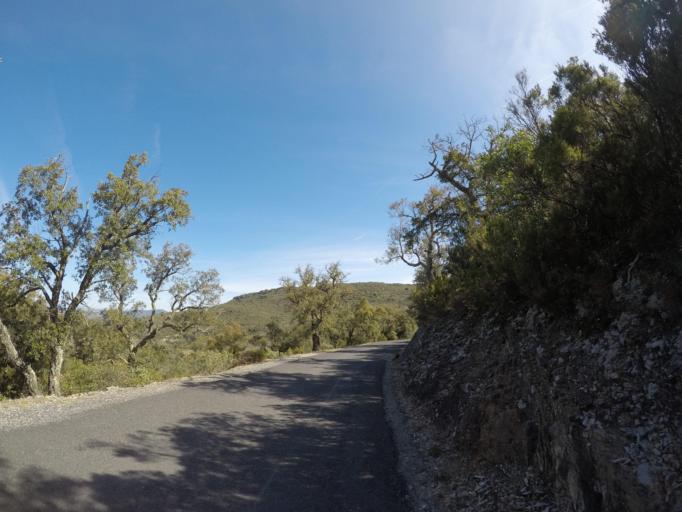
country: FR
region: Languedoc-Roussillon
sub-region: Departement des Pyrenees-Orientales
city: Thuir
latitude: 42.6239
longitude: 2.7037
